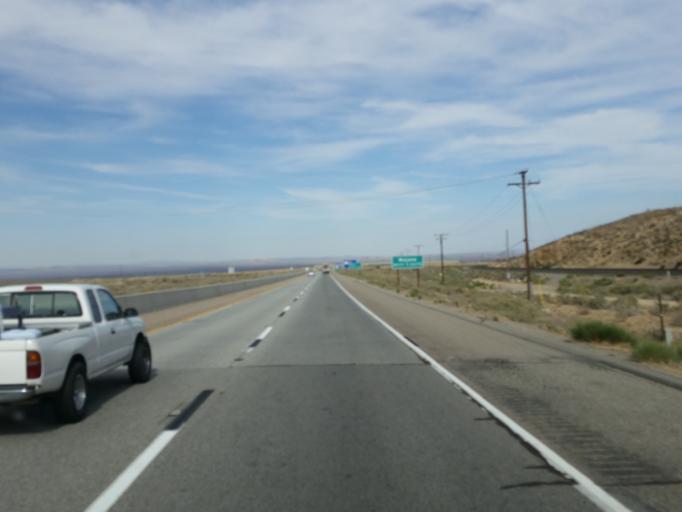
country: US
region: California
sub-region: Kern County
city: Mojave
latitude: 35.1166
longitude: -118.2002
